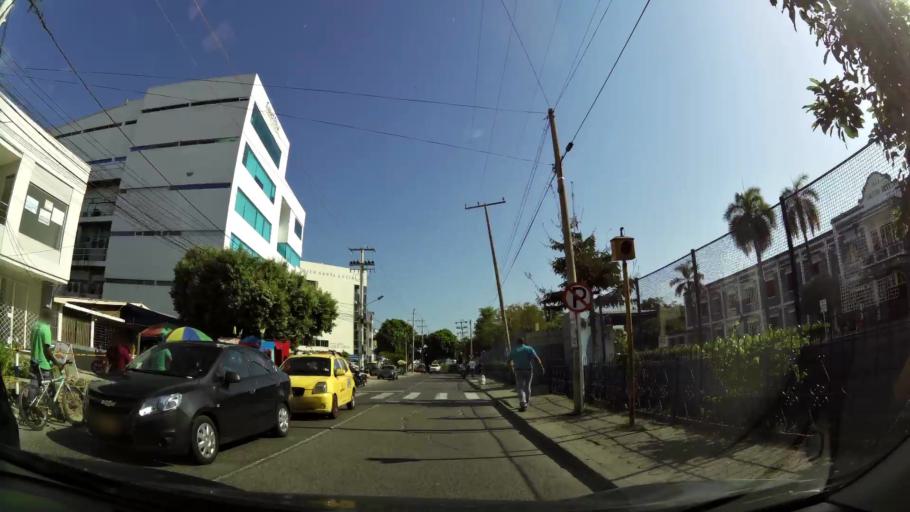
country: CO
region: Bolivar
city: Cartagena
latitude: 10.3928
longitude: -75.4782
